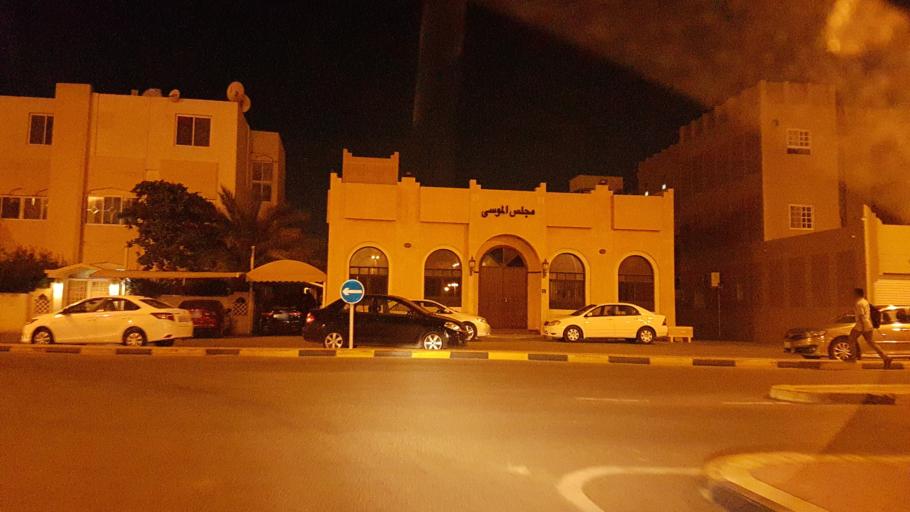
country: BH
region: Muharraq
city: Al Hadd
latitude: 26.2451
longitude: 50.6559
